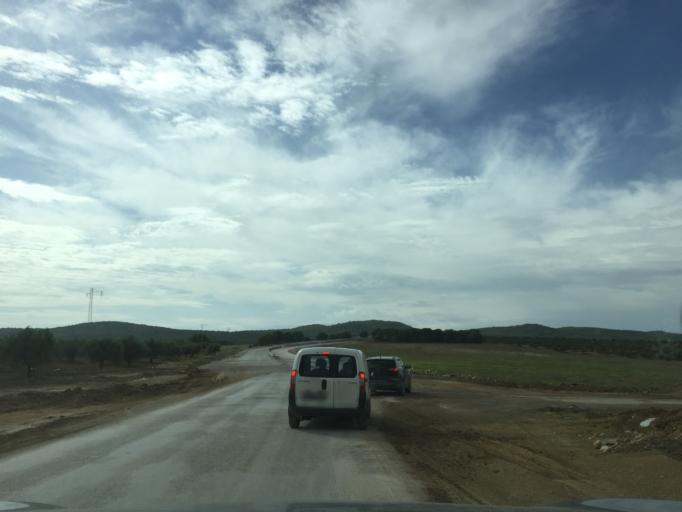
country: TN
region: Zaghwan
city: El Fahs
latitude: 36.2849
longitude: 9.8065
